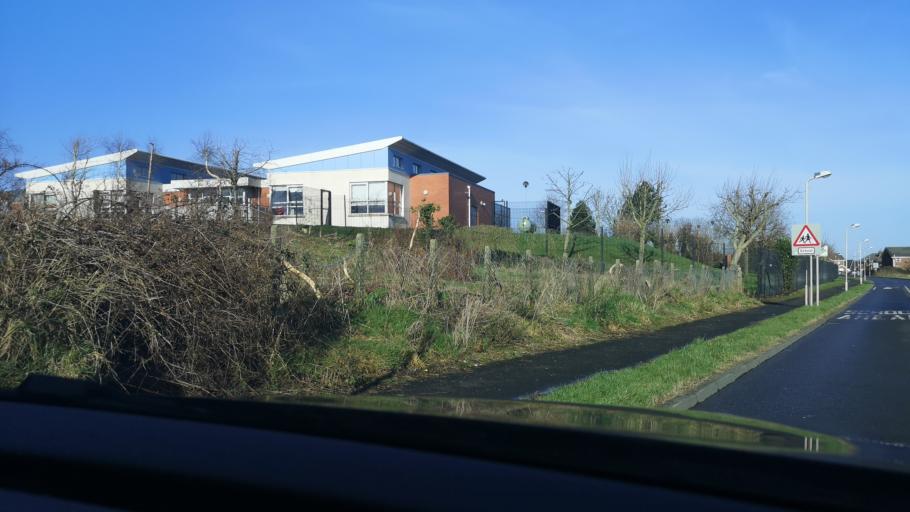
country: GB
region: Northern Ireland
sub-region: Newry and Mourne District
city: Newry
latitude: 54.1770
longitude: -6.3533
